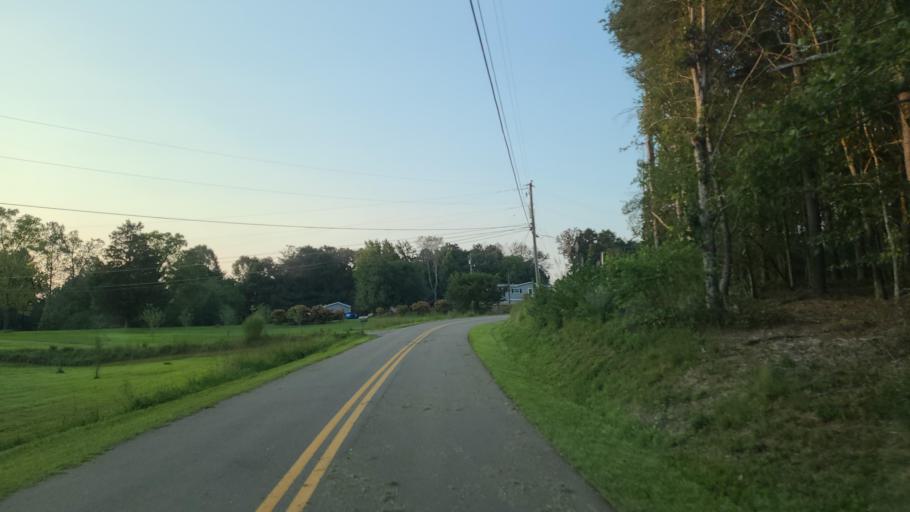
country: US
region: Georgia
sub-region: Pickens County
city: Jasper
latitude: 34.4629
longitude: -84.5422
